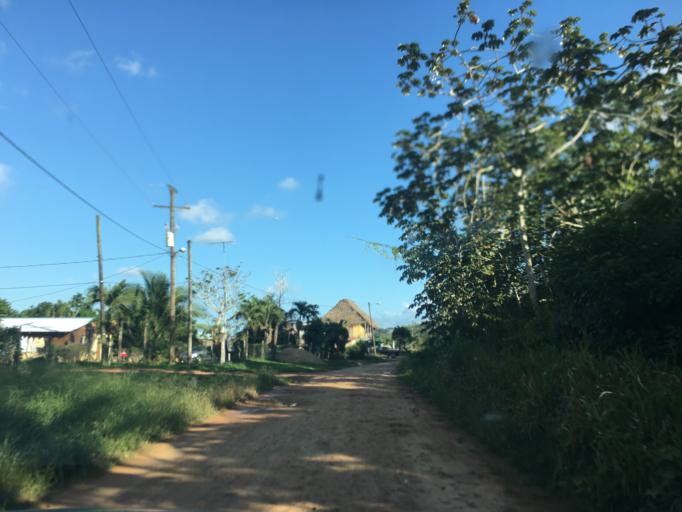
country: BZ
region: Stann Creek
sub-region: Dangriga
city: Dangriga
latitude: 16.7976
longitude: -88.3816
